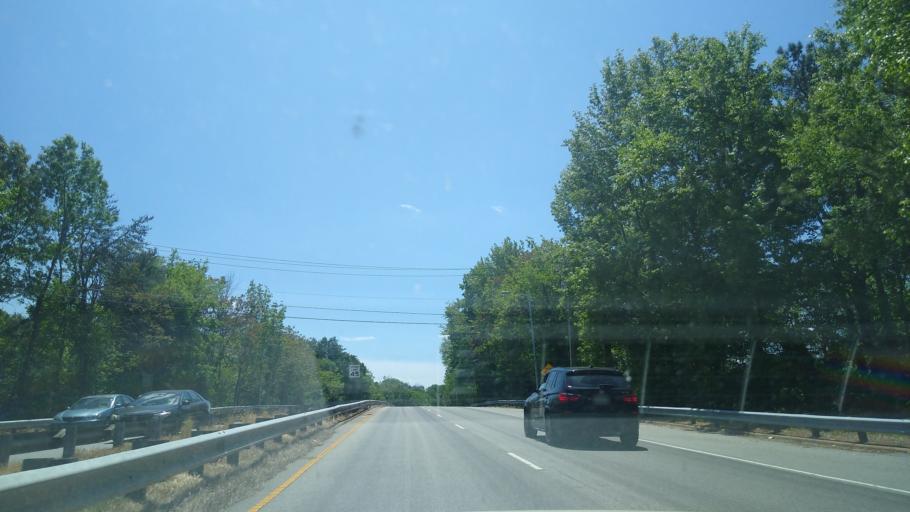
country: US
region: North Carolina
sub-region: Guilford County
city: Greensboro
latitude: 36.0757
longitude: -79.8311
